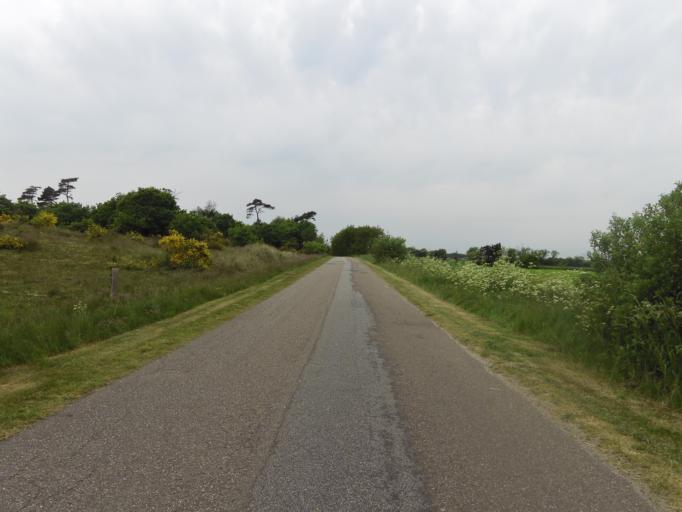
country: DK
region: South Denmark
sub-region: Esbjerg Kommune
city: Ribe
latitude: 55.3246
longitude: 8.8196
